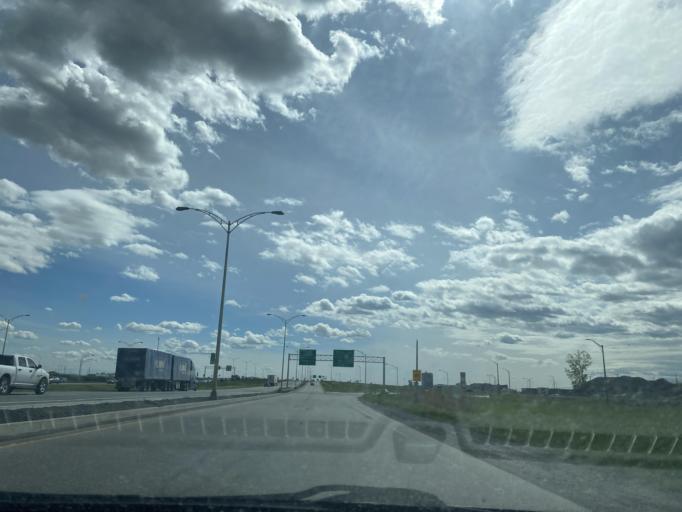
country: CA
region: Quebec
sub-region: Monteregie
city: Brossard
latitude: 45.4477
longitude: -73.4239
